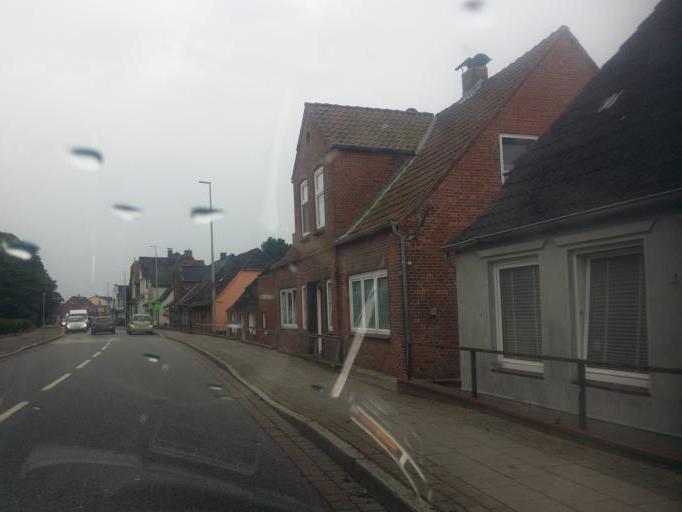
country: DE
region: Schleswig-Holstein
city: Husum
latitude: 54.4689
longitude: 9.0526
